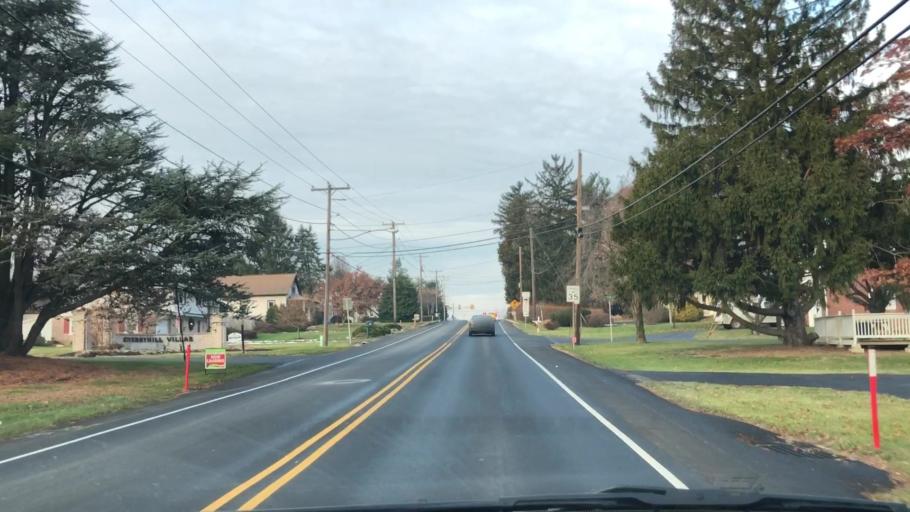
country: US
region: Pennsylvania
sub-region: Lancaster County
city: Mountville
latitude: 40.0571
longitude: -76.3955
